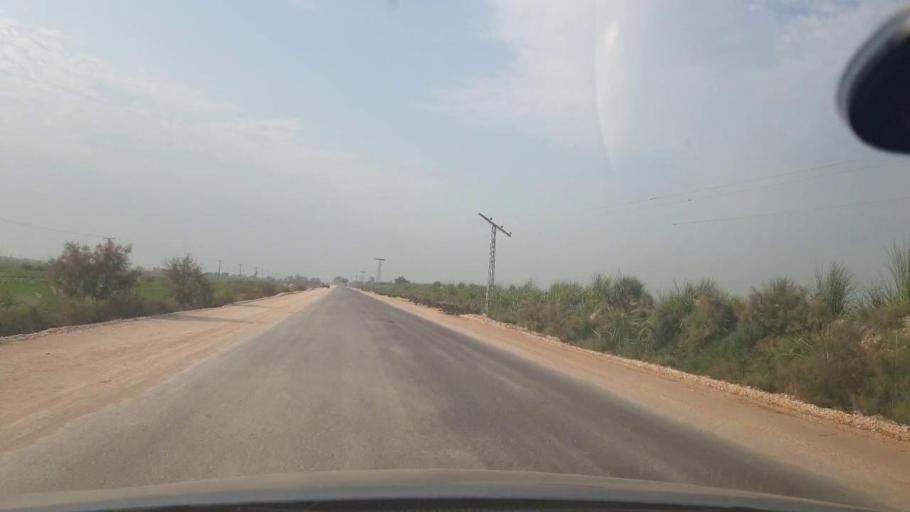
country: PK
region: Sindh
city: Jacobabad
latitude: 28.1816
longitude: 68.3675
